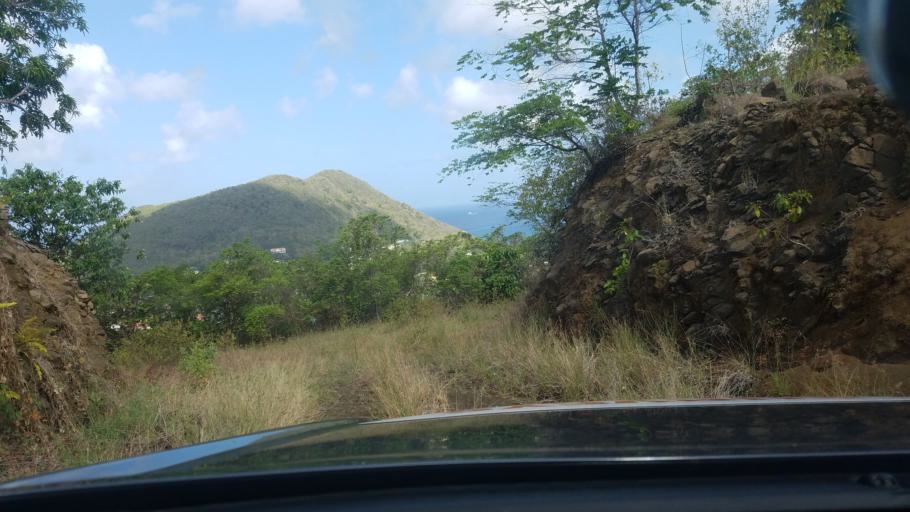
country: LC
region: Gros-Islet
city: Gros Islet
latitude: 14.0648
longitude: -60.9484
